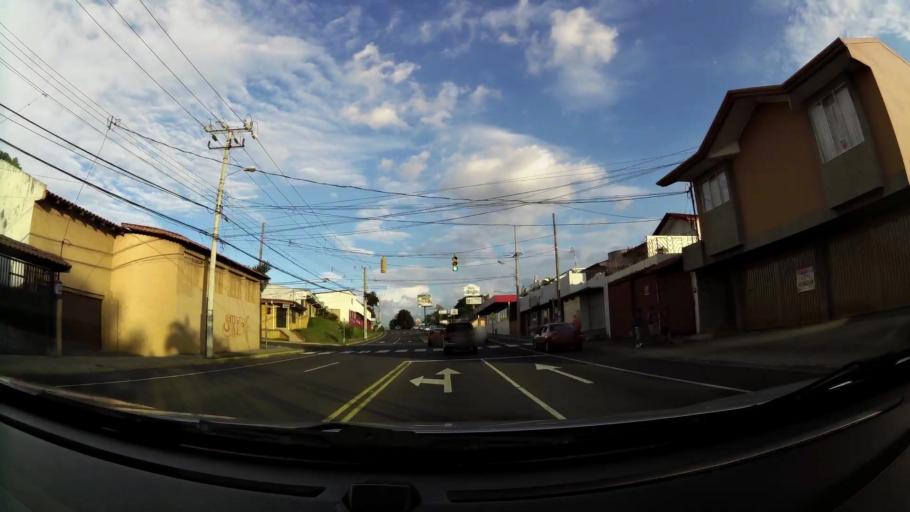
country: CR
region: Heredia
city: San Francisco
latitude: 9.9964
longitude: -84.1341
